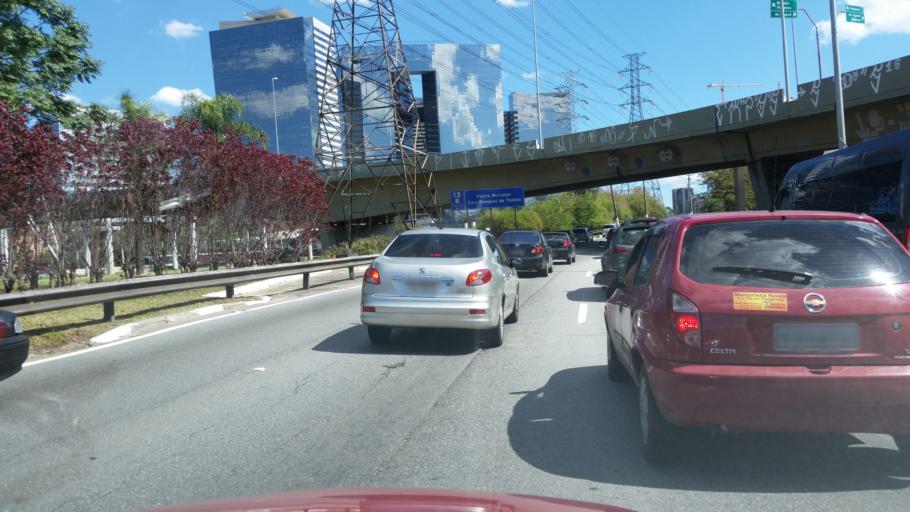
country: BR
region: Sao Paulo
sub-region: Taboao Da Serra
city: Taboao da Serra
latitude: -23.6189
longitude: -46.7018
